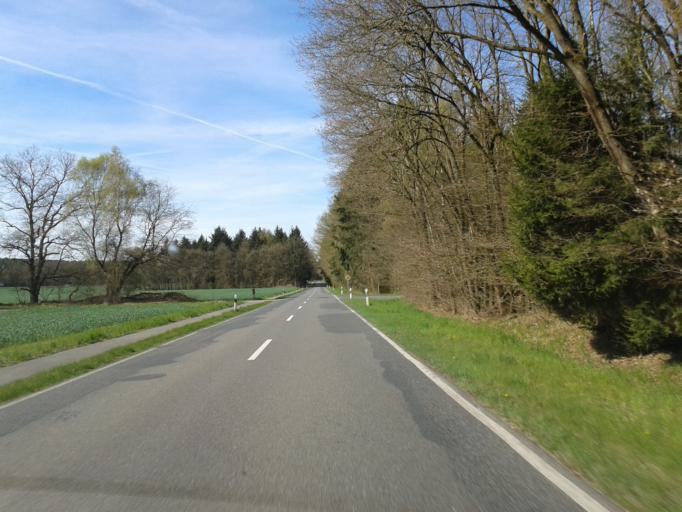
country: DE
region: Lower Saxony
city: Schnega
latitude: 52.9246
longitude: 10.8818
